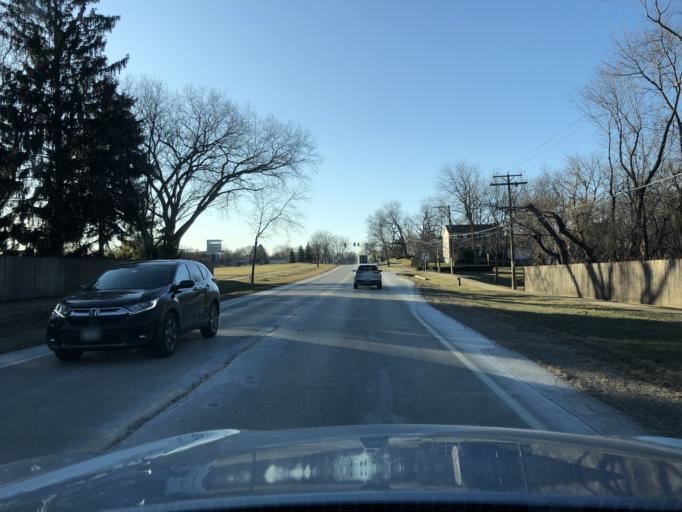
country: US
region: Illinois
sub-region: Cook County
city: Barrington
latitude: 42.1542
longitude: -88.1170
